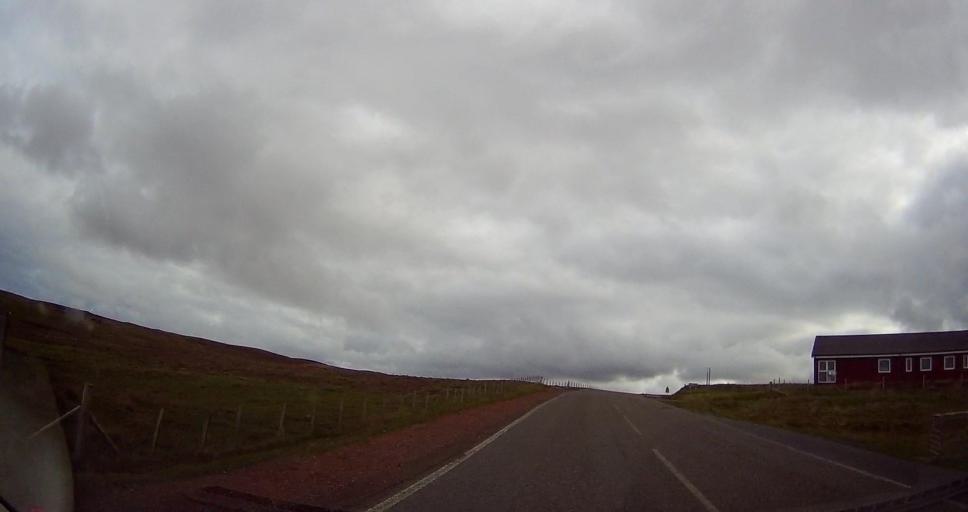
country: GB
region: Scotland
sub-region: Shetland Islands
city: Shetland
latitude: 60.6613
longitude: -1.0455
